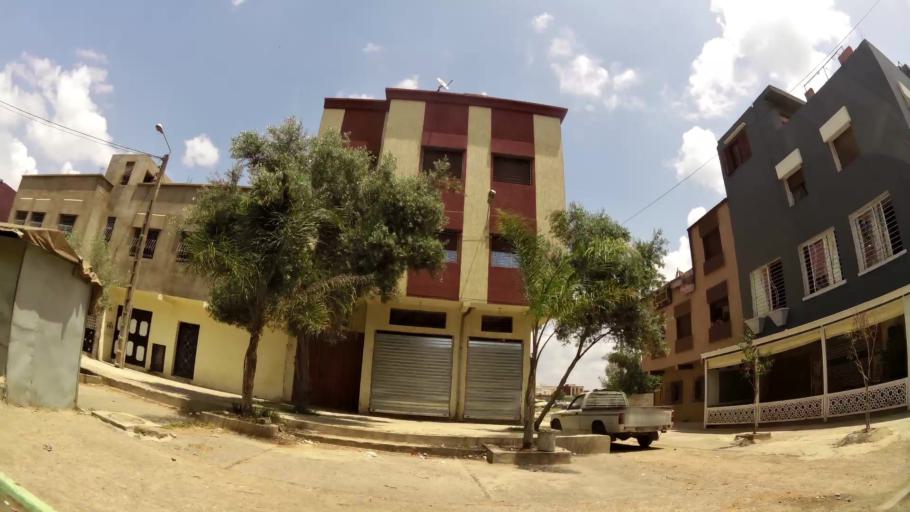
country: MA
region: Rabat-Sale-Zemmour-Zaer
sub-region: Khemisset
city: Tiflet
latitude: 34.0020
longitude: -6.5293
